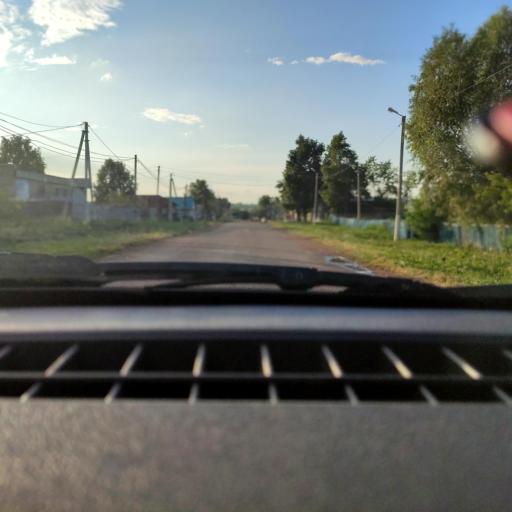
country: RU
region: Bashkortostan
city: Blagoveshchensk
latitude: 55.0944
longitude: 55.8589
